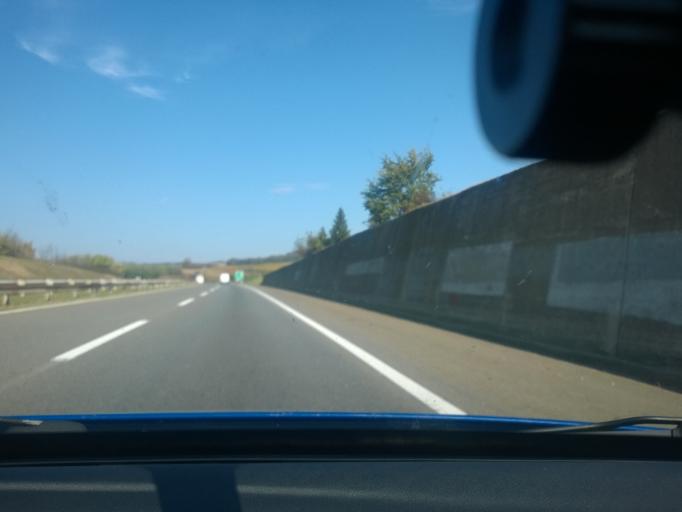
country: RS
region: Central Serbia
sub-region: Nisavski Okrug
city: Razanj
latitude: 43.6500
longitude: 21.5548
